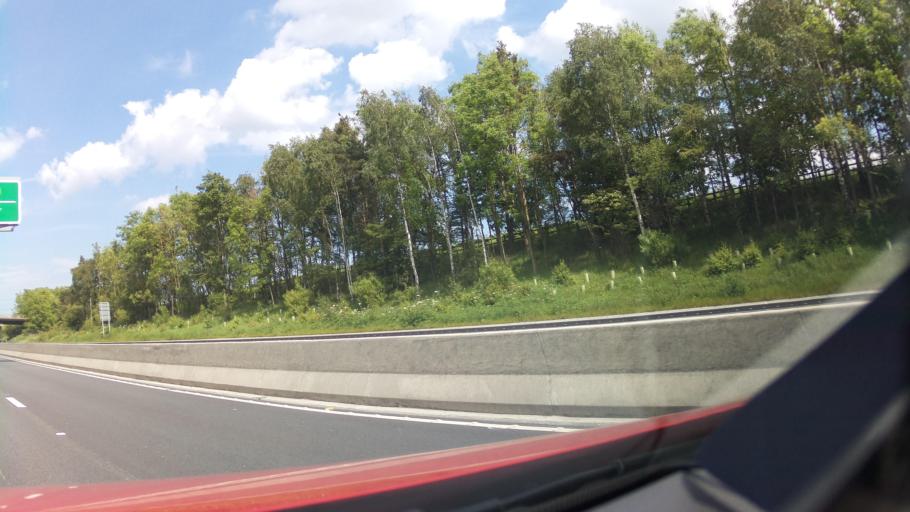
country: GB
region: England
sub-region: Stockton-on-Tees
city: Billingham
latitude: 54.6198
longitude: -1.3167
